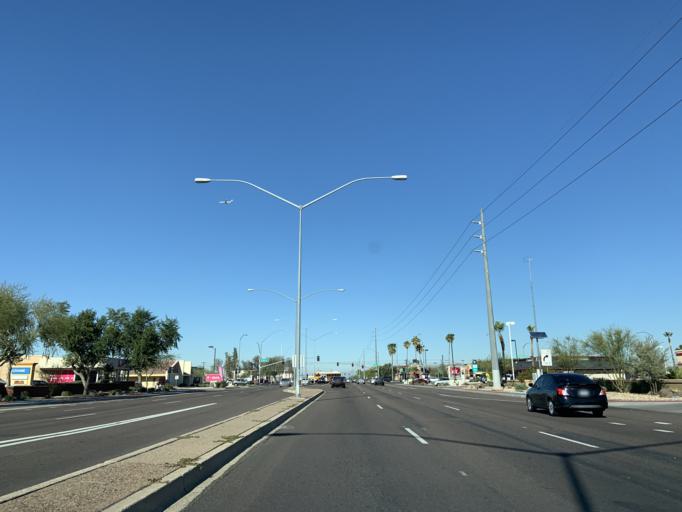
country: US
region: Arizona
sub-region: Maricopa County
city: Tempe
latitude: 33.4134
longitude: -111.8744
